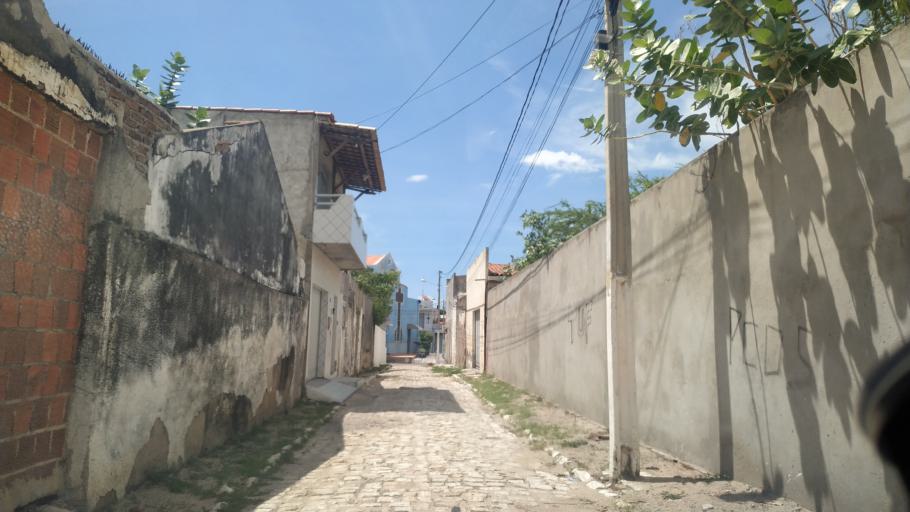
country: BR
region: Rio Grande do Norte
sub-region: Areia Branca
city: Areia Branca
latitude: -4.9568
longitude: -37.1365
